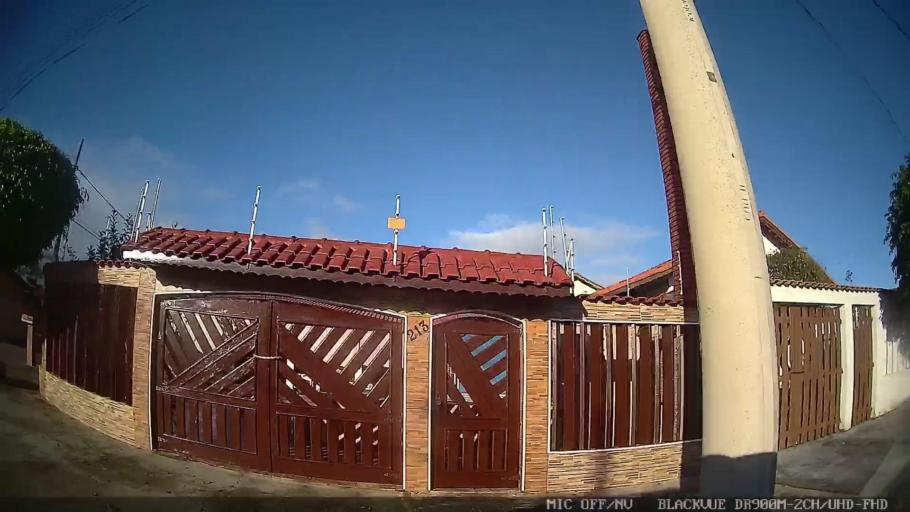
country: BR
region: Sao Paulo
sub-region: Itanhaem
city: Itanhaem
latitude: -24.2422
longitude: -46.8891
